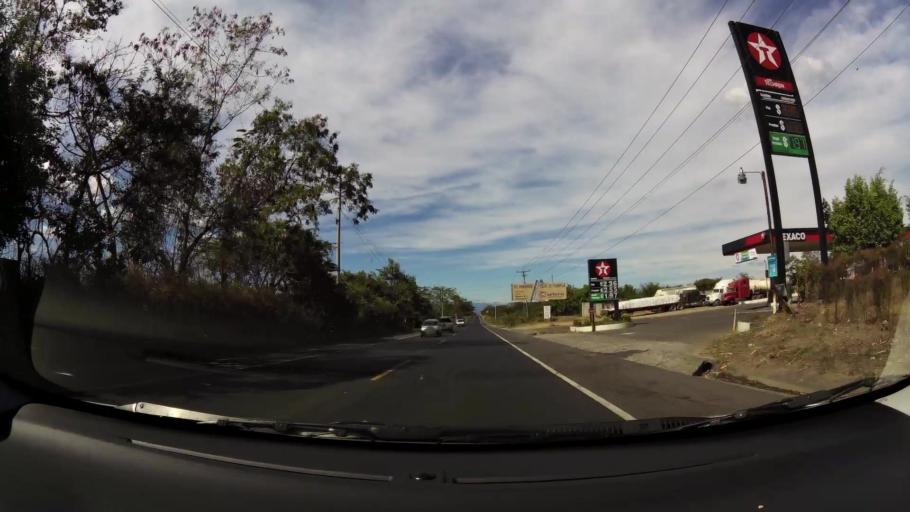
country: SV
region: San Salvador
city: Guazapa
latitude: 13.8901
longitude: -89.1766
